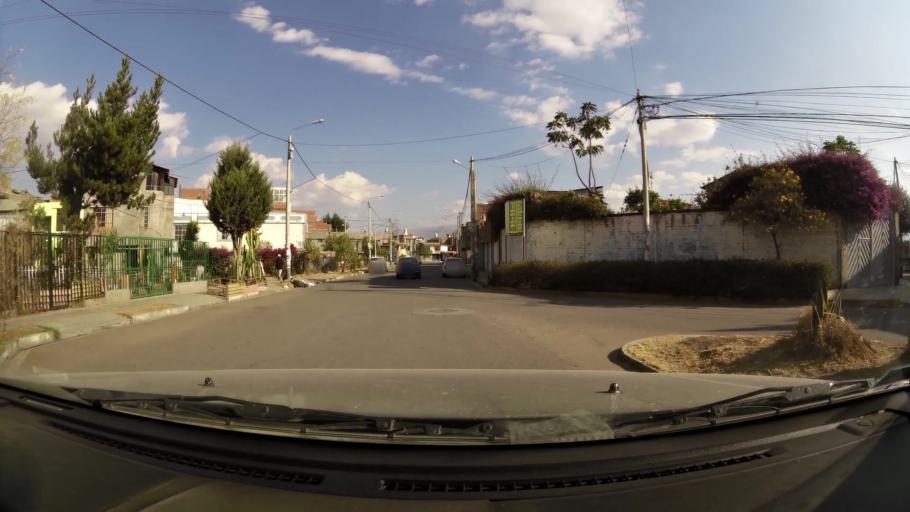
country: PE
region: Junin
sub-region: Provincia de Huancayo
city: El Tambo
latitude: -12.0606
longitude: -75.2246
